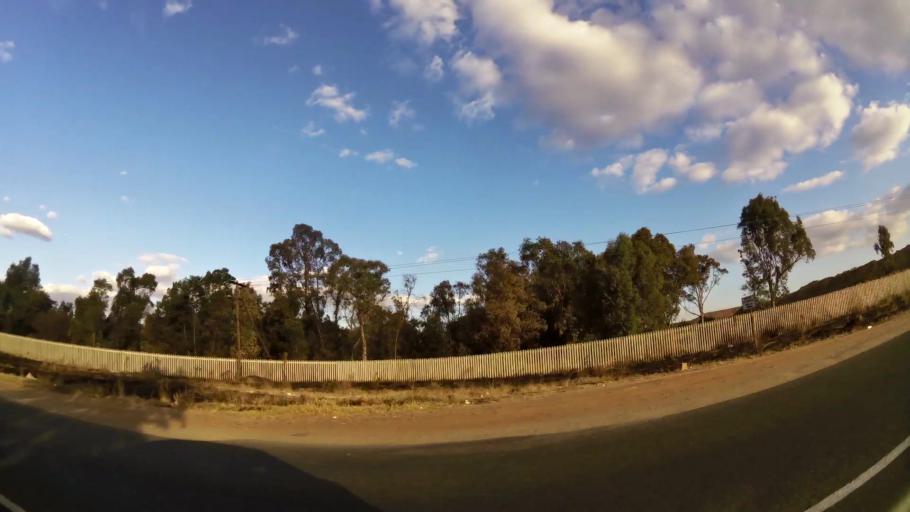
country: ZA
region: Gauteng
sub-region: Ekurhuleni Metropolitan Municipality
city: Tembisa
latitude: -25.9551
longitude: 28.1839
